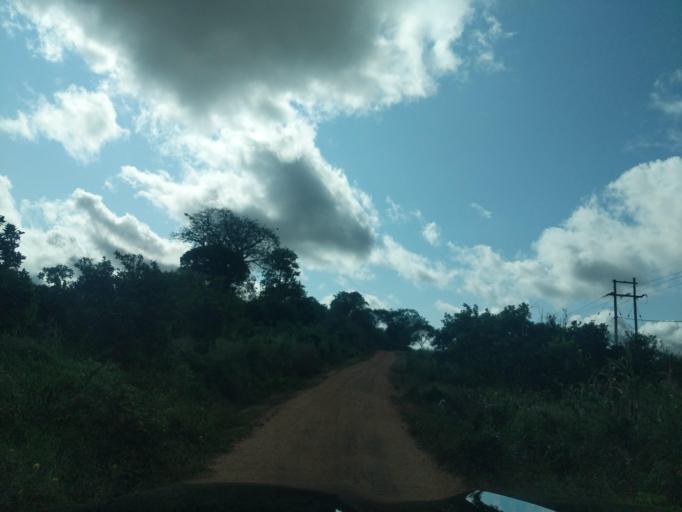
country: TZ
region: Tanga
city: Muheza
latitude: -5.4192
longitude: 38.6234
